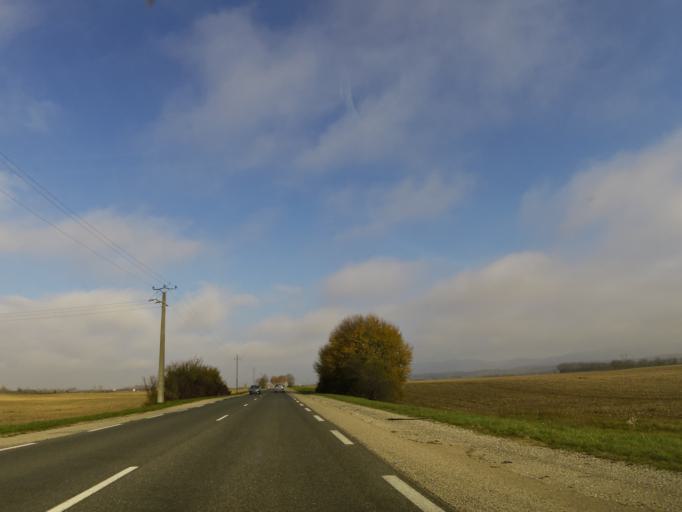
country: FR
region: Rhone-Alpes
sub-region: Departement de l'Ain
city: Chazey-sur-Ain
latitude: 45.9116
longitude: 5.2501
